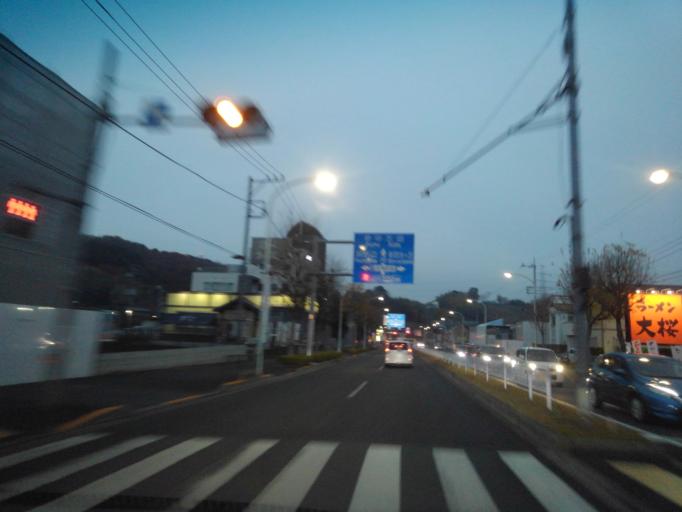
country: JP
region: Tokyo
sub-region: Machida-shi
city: Machida
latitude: 35.5861
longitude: 139.4498
